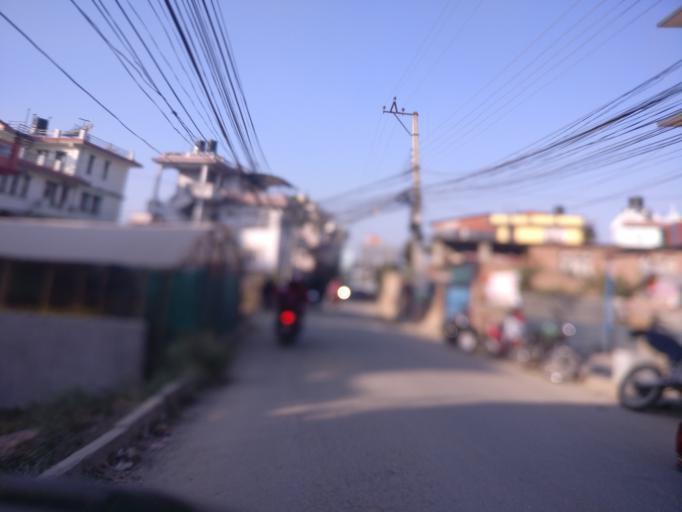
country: NP
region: Central Region
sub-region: Bagmati Zone
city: Patan
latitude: 27.6550
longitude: 85.3170
